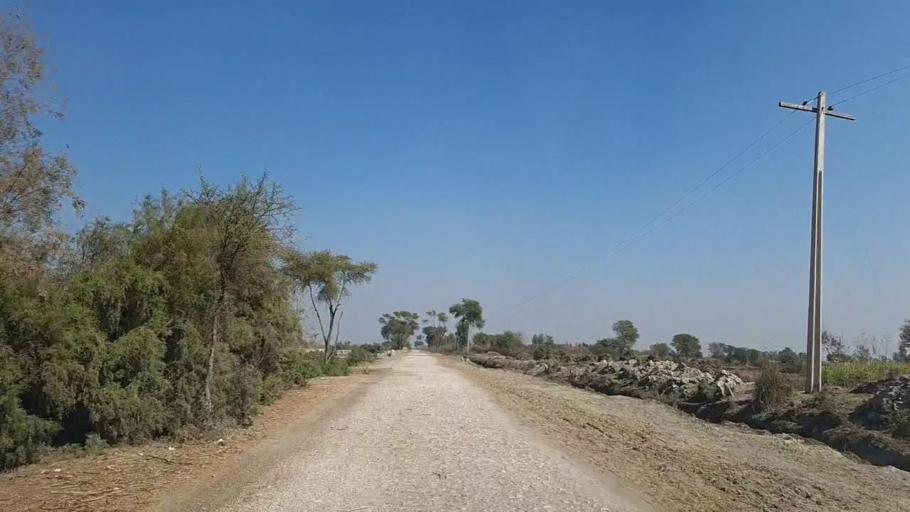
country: PK
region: Sindh
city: Bandhi
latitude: 26.5420
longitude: 68.3239
